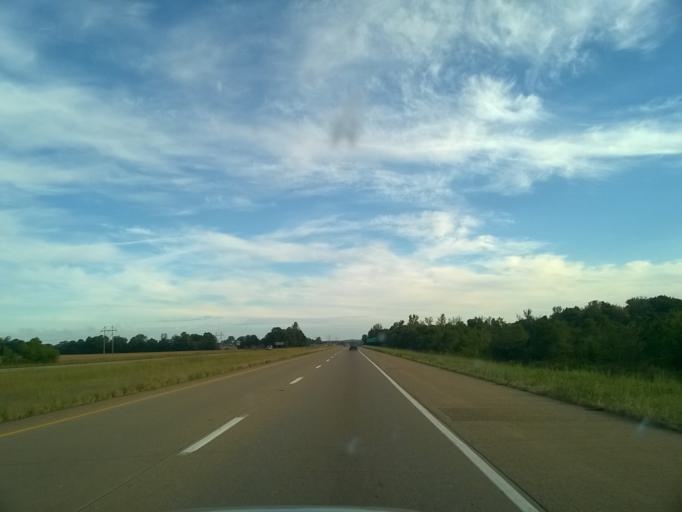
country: US
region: Indiana
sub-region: Vanderburgh County
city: Melody Hill
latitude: 38.0729
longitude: -87.4760
